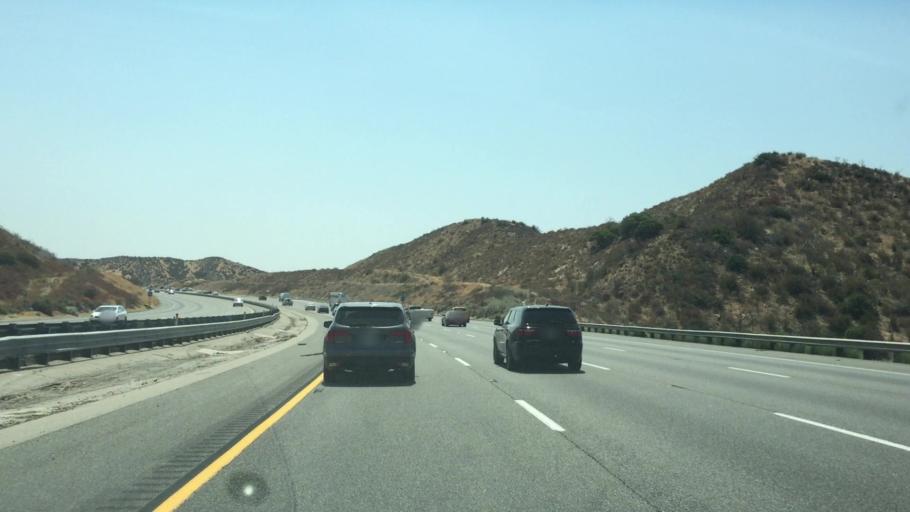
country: US
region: California
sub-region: Los Angeles County
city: Castaic
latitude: 34.6410
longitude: -118.7493
